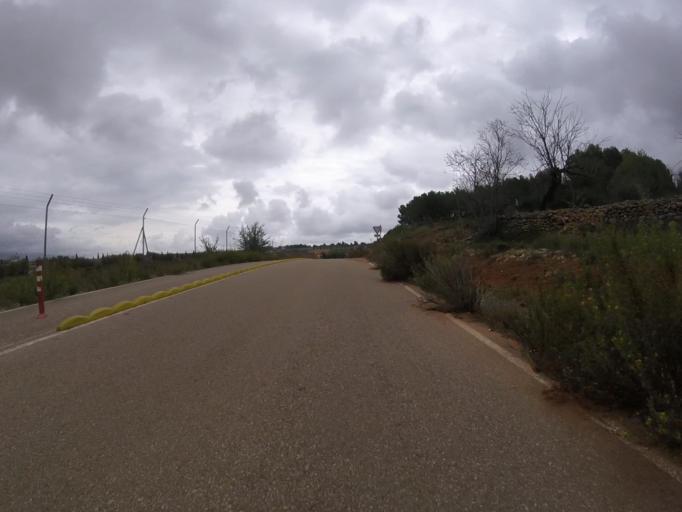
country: ES
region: Valencia
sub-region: Provincia de Castello
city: Benlloch
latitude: 40.1943
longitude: 0.0518
